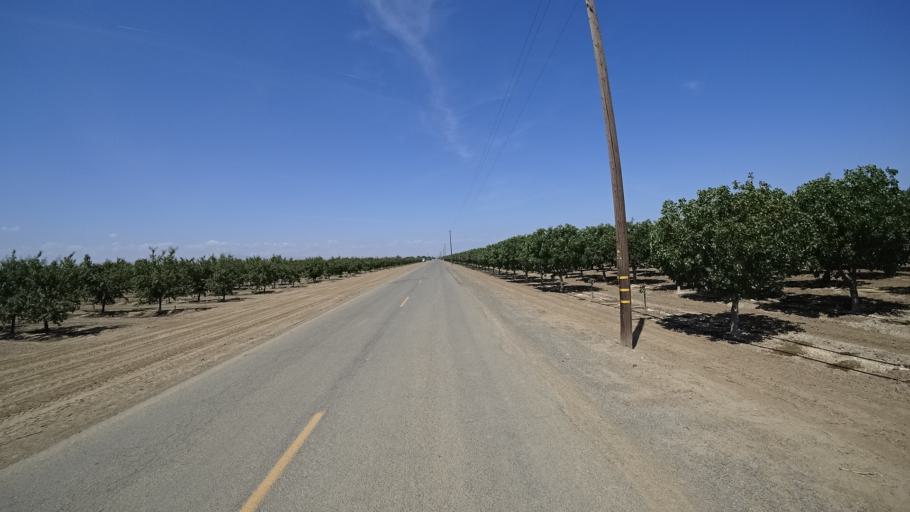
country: US
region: California
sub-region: Kings County
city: Kettleman City
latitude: 36.0943
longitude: -119.9887
